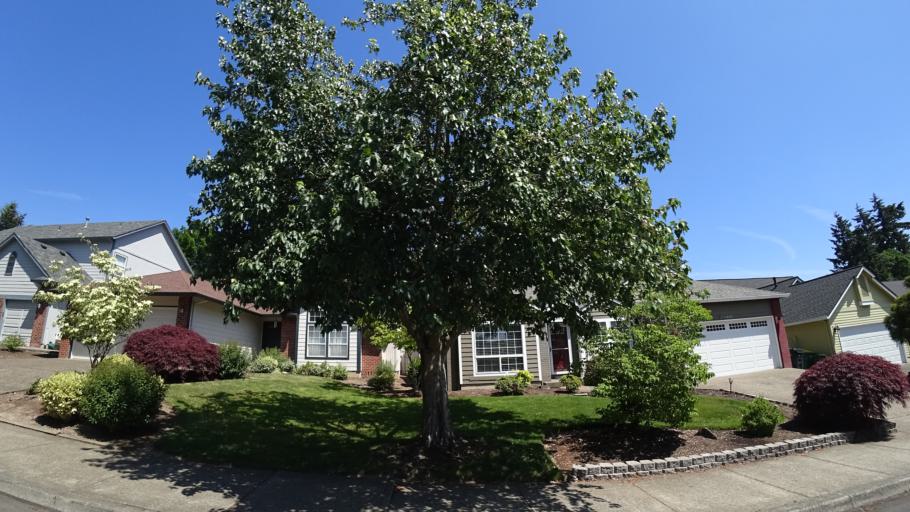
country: US
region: Oregon
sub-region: Washington County
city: King City
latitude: 45.4399
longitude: -122.8105
